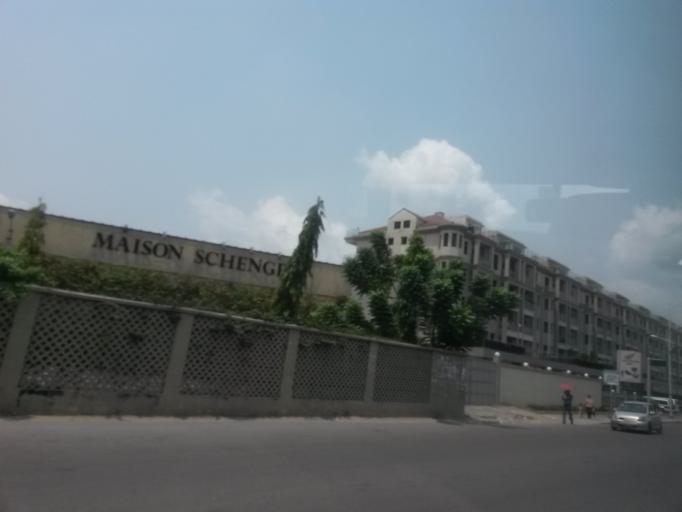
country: CD
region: Kinshasa
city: Kinshasa
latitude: -4.3184
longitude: 15.2933
